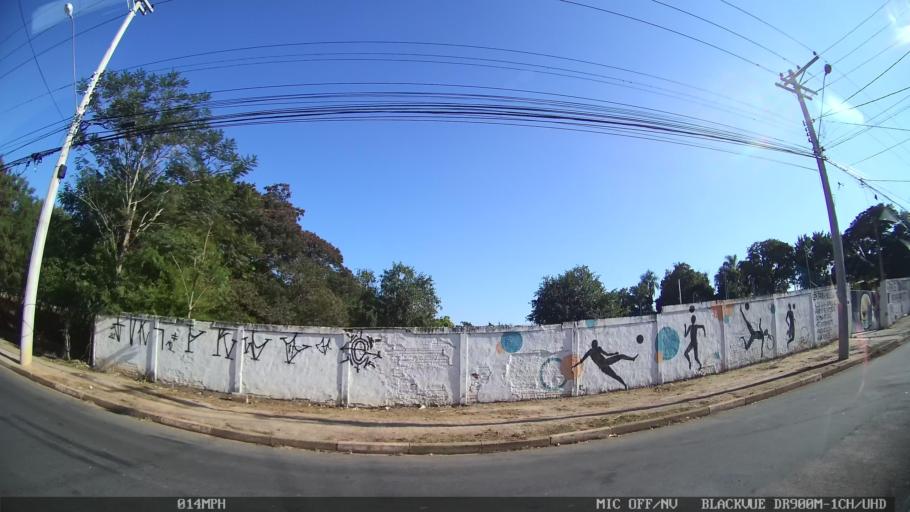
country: BR
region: Sao Paulo
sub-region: Campinas
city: Campinas
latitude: -22.9603
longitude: -47.1057
